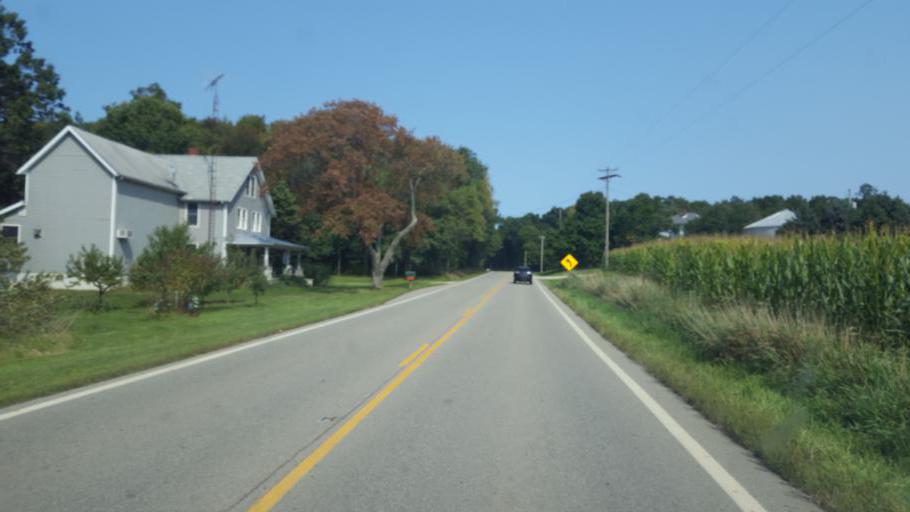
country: US
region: Ohio
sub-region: Wayne County
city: Shreve
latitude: 40.7176
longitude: -82.0664
